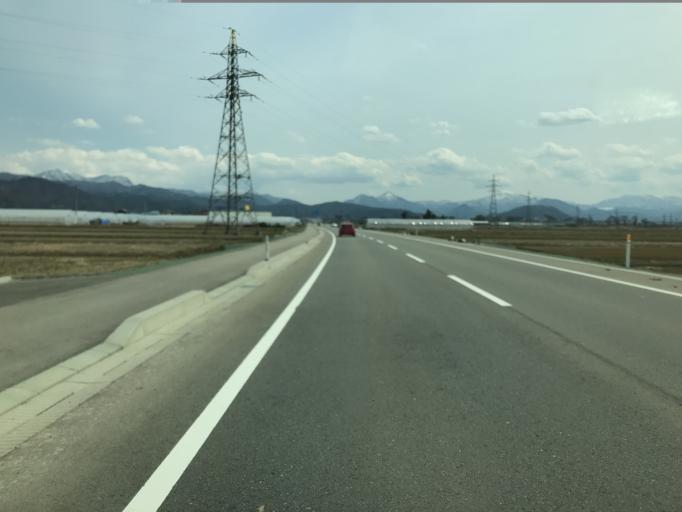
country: JP
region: Yamagata
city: Higashine
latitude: 38.4514
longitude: 140.3673
